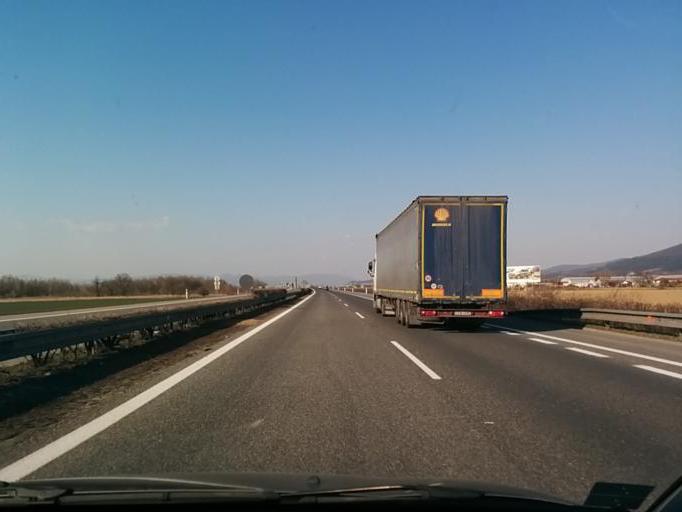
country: SK
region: Trenciansky
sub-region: Okres Nove Mesto nad Vahom
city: Nove Mesto nad Vahom
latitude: 48.7126
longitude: 17.8734
